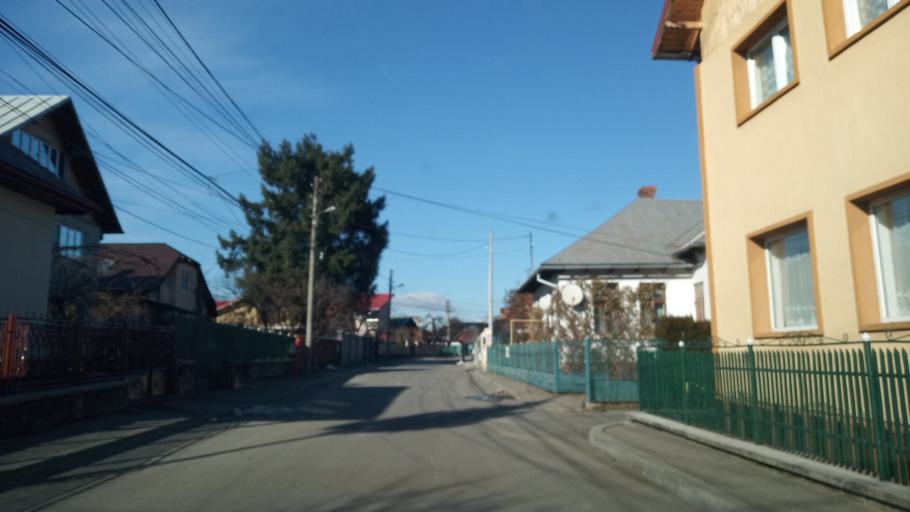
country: RO
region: Prahova
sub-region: Oras Breaza
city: Breaza
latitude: 45.1868
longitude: 25.6667
